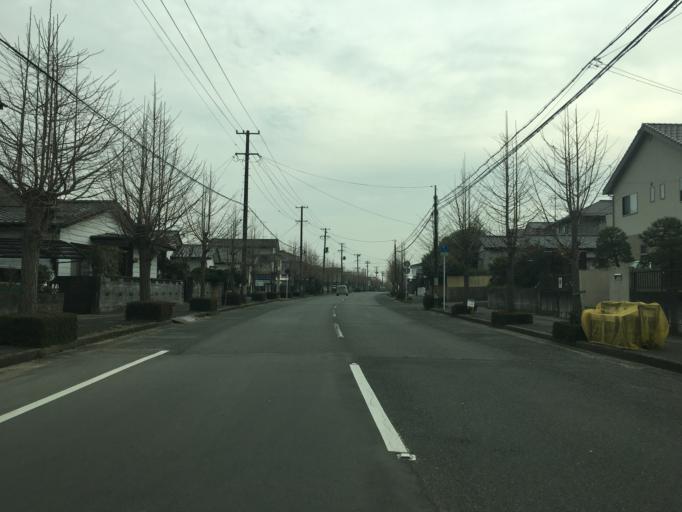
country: JP
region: Fukushima
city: Iwaki
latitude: 36.9862
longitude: 140.8864
